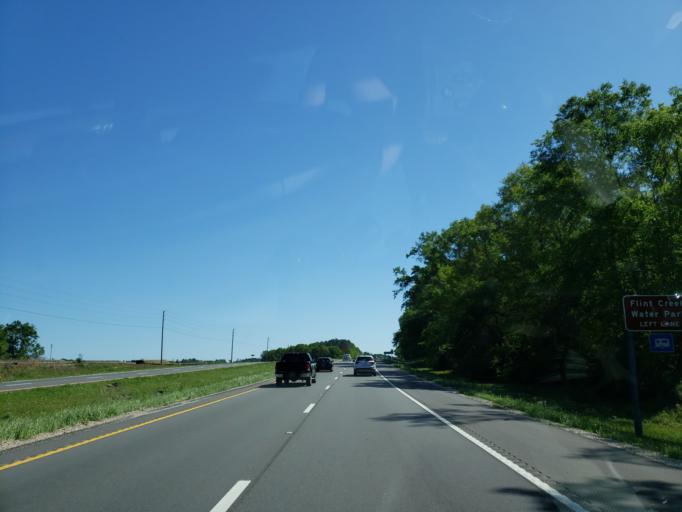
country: US
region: Mississippi
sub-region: Stone County
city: Wiggins
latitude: 30.8873
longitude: -89.1649
